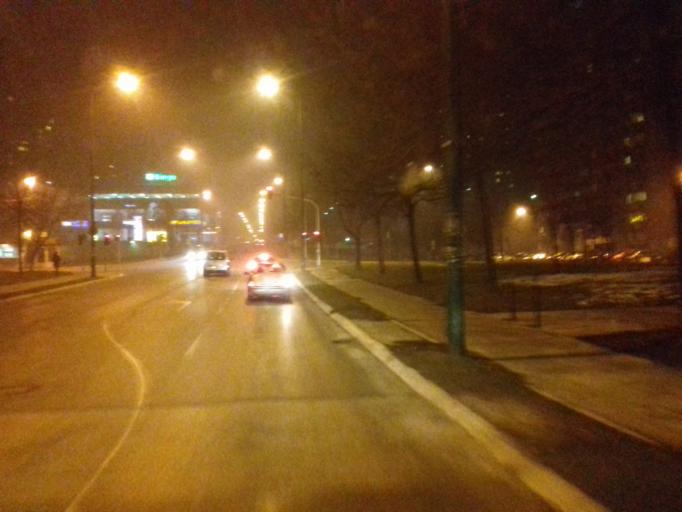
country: BA
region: Federation of Bosnia and Herzegovina
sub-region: Kanton Sarajevo
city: Sarajevo
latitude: 43.8456
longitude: 18.3475
